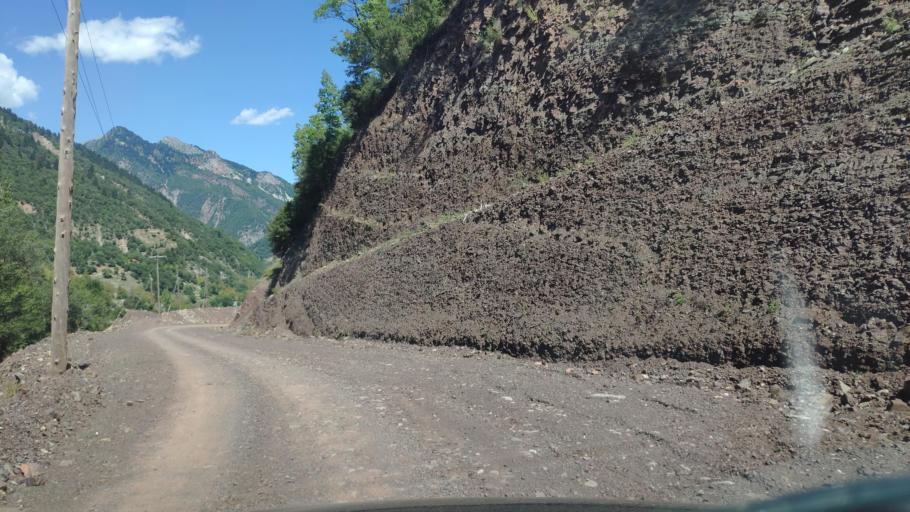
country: GR
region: Central Greece
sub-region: Nomos Evrytanias
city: Kerasochori
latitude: 39.1231
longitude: 21.6258
